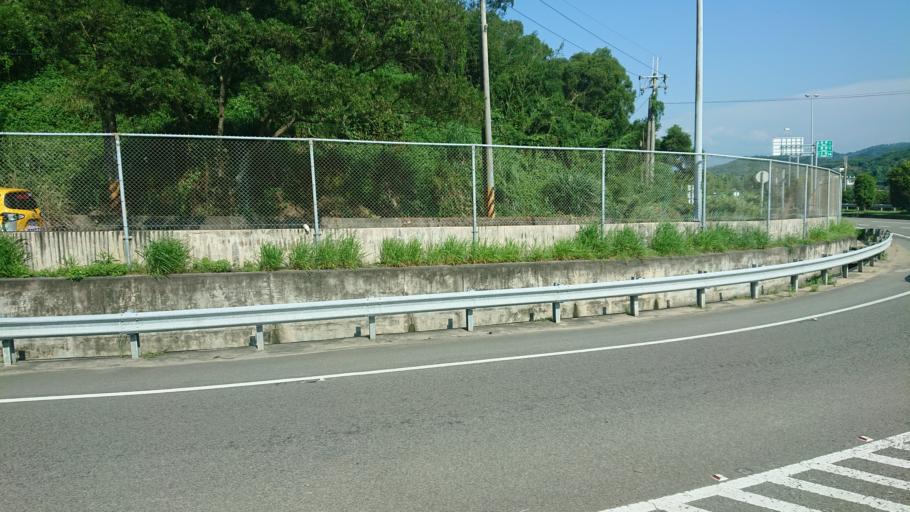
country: TW
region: Taiwan
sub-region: Miaoli
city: Miaoli
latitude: 24.5980
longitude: 120.7866
